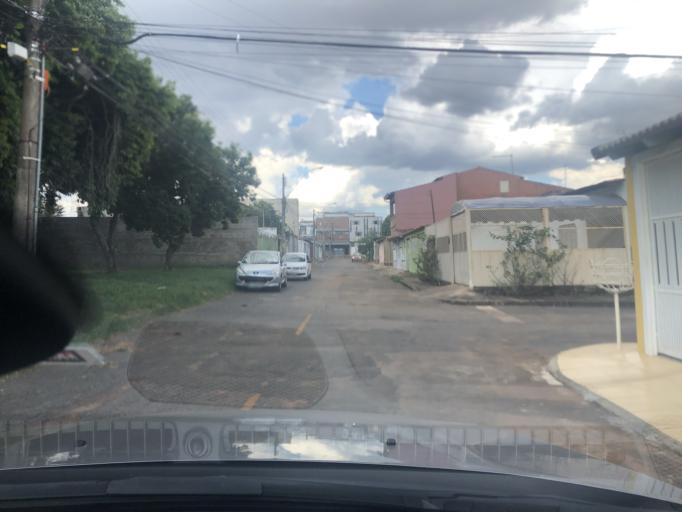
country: BR
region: Goias
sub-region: Luziania
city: Luziania
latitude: -16.0244
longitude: -48.0623
